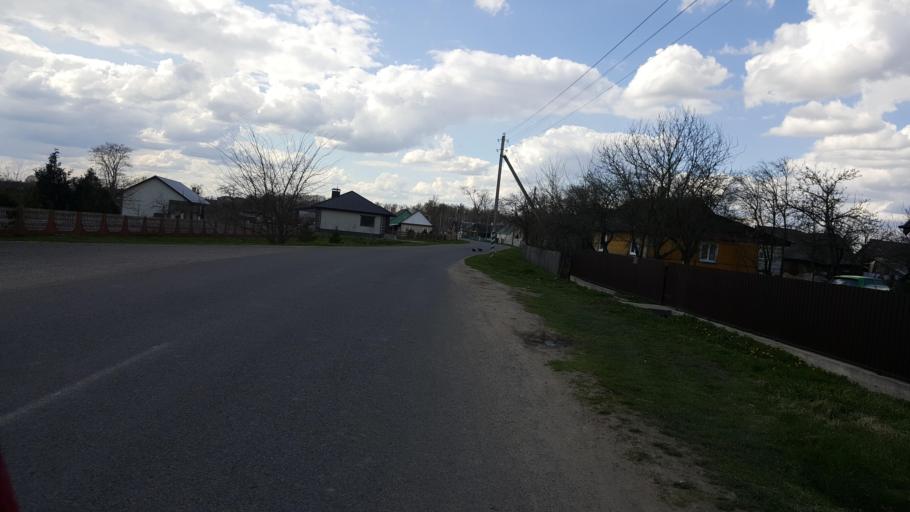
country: BY
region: Brest
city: Kamyanyets
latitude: 52.4101
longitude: 23.6255
